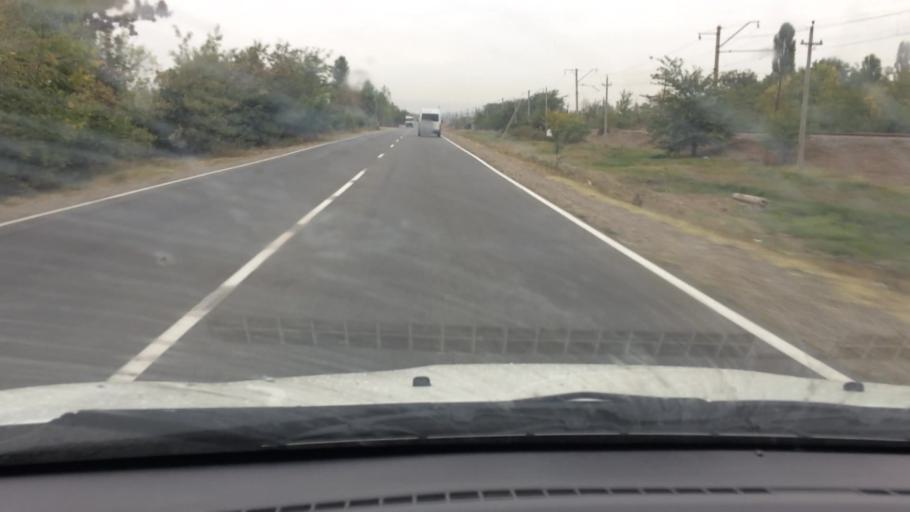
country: GE
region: Kvemo Kartli
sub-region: Marneuli
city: Marneuli
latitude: 41.4522
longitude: 44.8131
